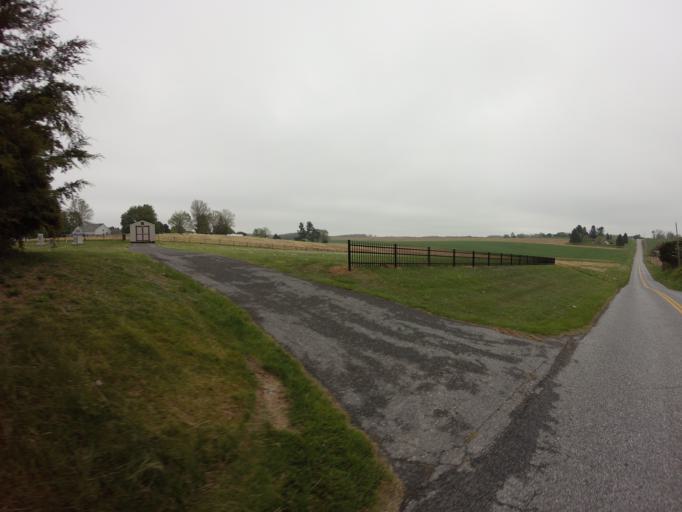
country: US
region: Maryland
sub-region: Baltimore County
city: Hunt Valley
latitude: 39.5827
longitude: -76.7170
